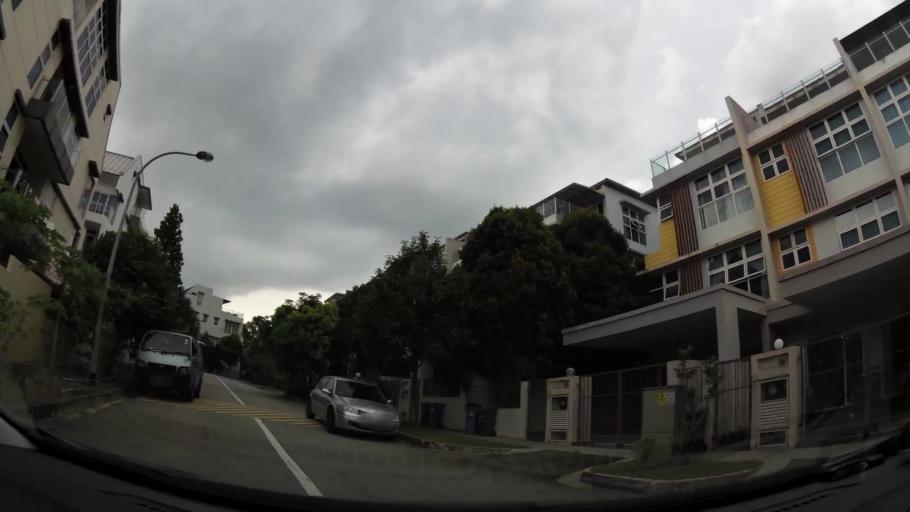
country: MY
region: Johor
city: Kampung Pasir Gudang Baru
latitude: 1.4597
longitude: 103.8386
